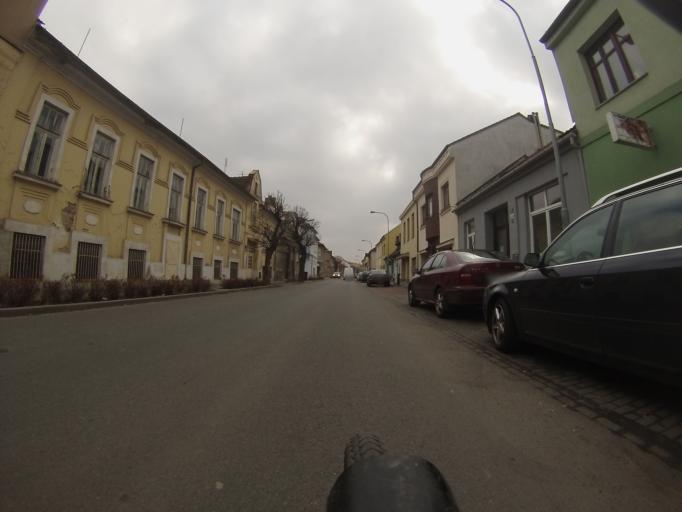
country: CZ
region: South Moravian
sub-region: Mesto Brno
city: Brno
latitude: 49.1992
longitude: 16.6413
